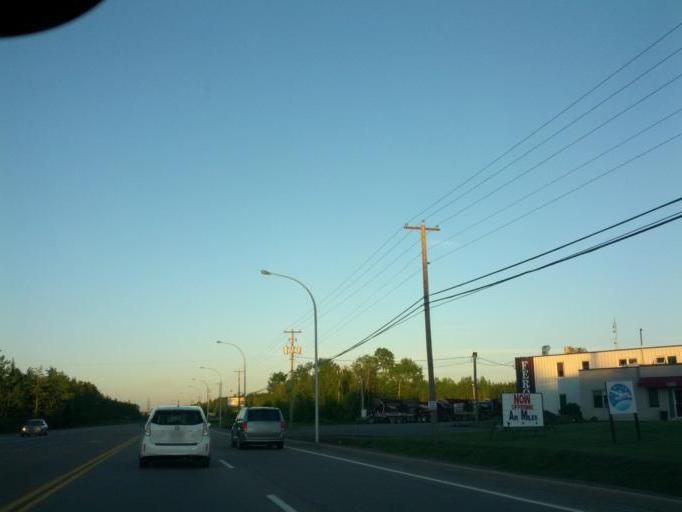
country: CA
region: New Brunswick
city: Moncton
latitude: 46.0976
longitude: -64.8596
